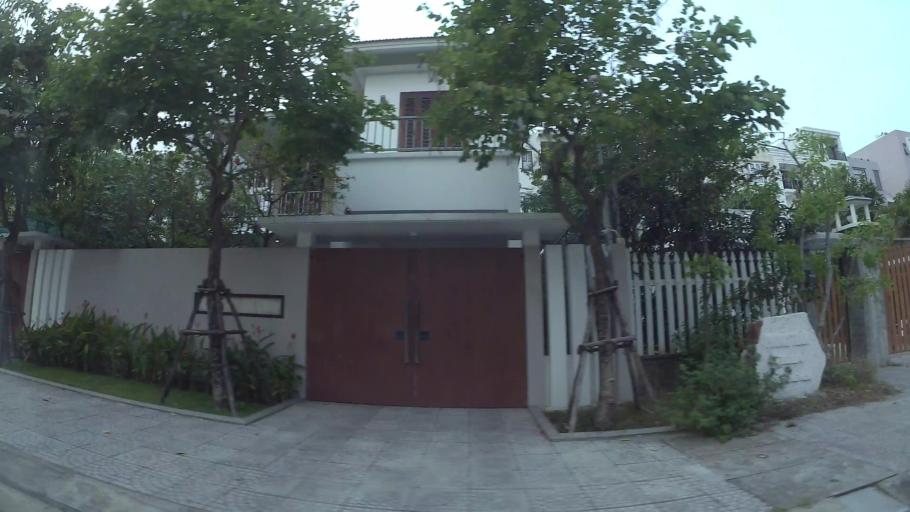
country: VN
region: Da Nang
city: Son Tra
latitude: 16.0490
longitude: 108.2444
